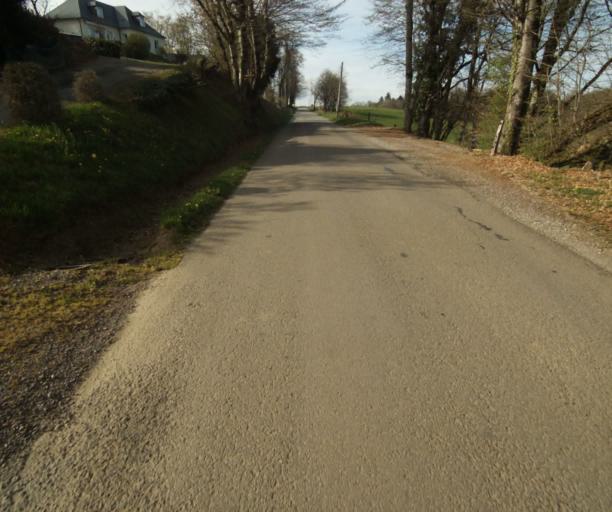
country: FR
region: Limousin
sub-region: Departement de la Correze
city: Naves
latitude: 45.2988
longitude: 1.7397
